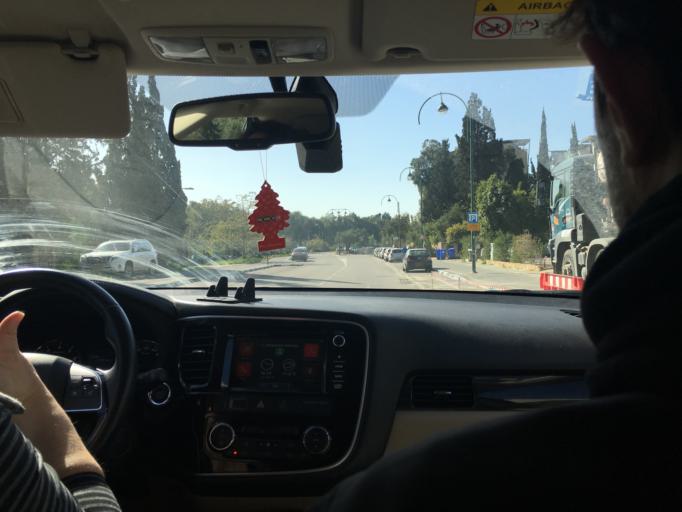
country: IL
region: Tel Aviv
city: Ramat HaSharon
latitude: 32.1422
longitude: 34.8467
